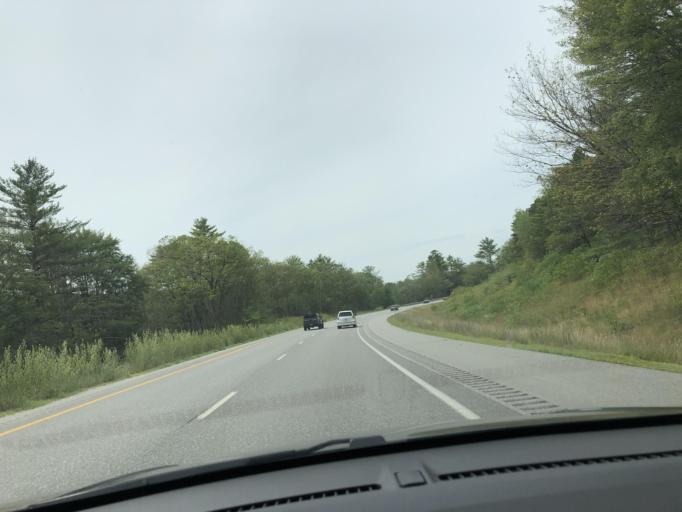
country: US
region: New Hampshire
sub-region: Merrimack County
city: Contoocook
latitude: 43.2688
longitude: -71.7774
